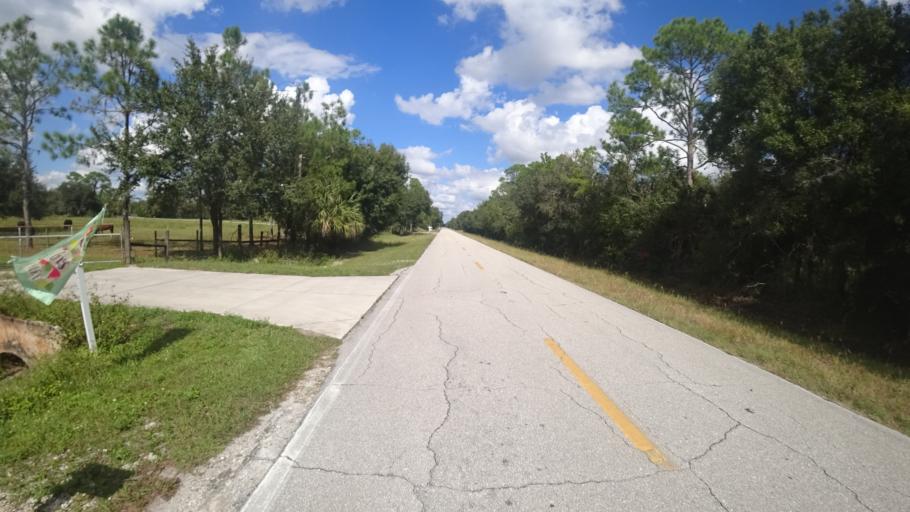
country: US
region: Florida
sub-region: Sarasota County
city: Warm Mineral Springs
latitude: 27.2642
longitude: -82.1196
